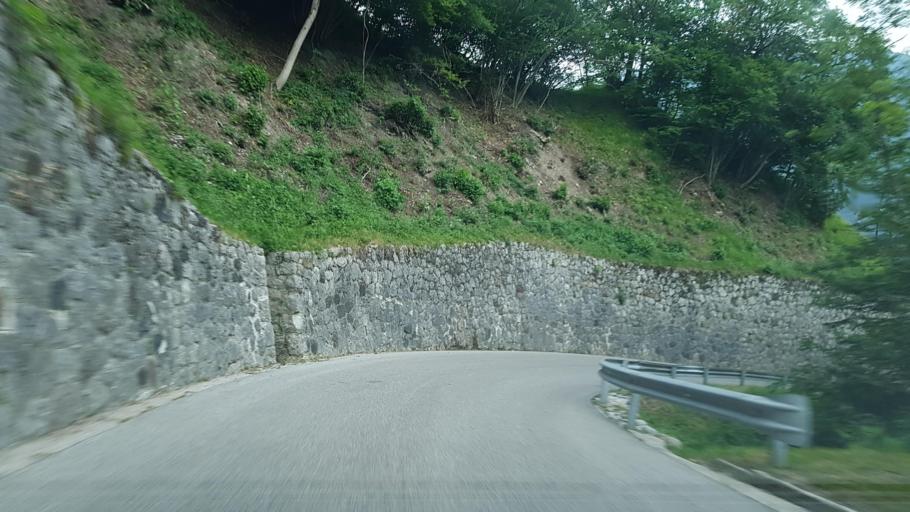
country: IT
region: Friuli Venezia Giulia
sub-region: Provincia di Udine
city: Pontebba
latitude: 46.5117
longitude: 13.3002
